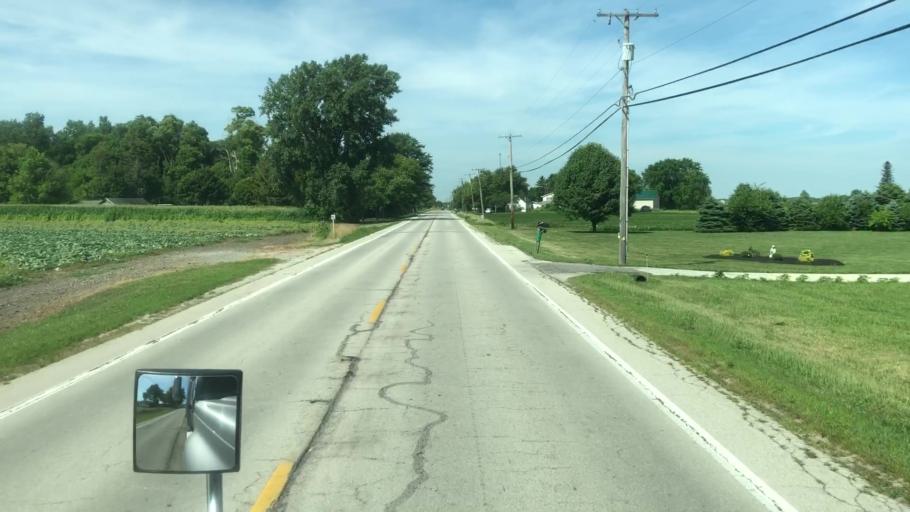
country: US
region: Ohio
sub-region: Ottawa County
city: Port Clinton
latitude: 41.4118
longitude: -82.9072
